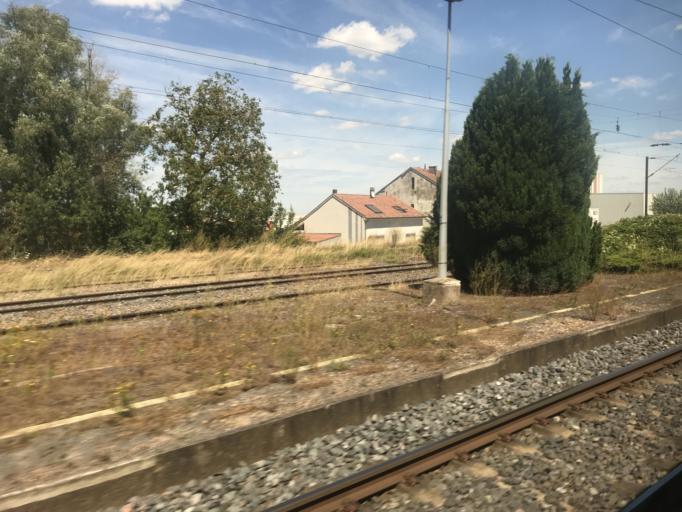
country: FR
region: Lorraine
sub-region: Departement de la Moselle
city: Dieuze
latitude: 48.9067
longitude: 6.7520
